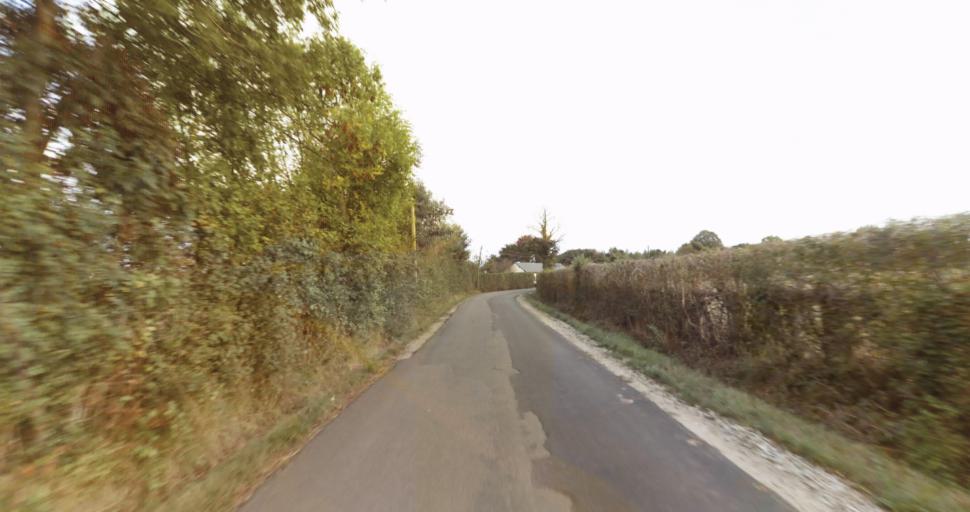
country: FR
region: Lower Normandy
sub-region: Departement de l'Orne
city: Vimoutiers
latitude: 48.8997
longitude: 0.1367
